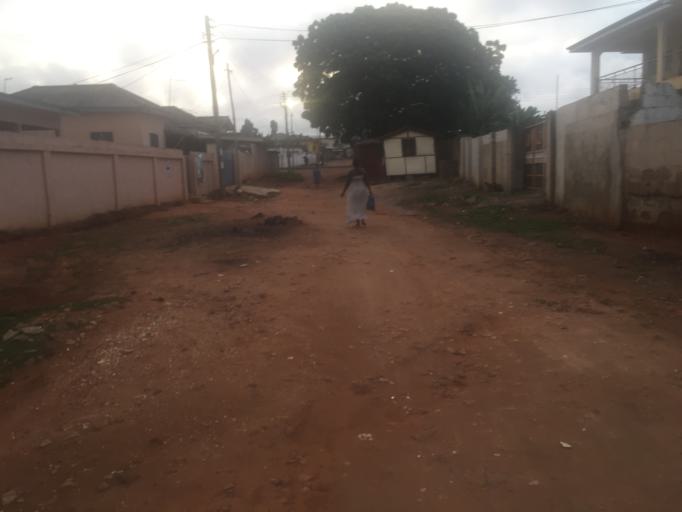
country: GH
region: Greater Accra
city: Dome
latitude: 5.6042
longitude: -0.2234
